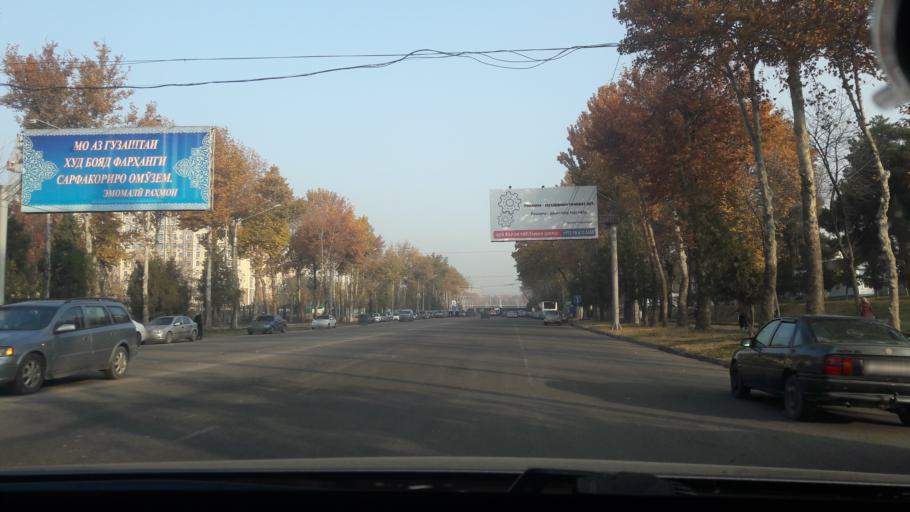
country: TJ
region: Dushanbe
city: Dushanbe
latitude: 38.5785
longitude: 68.7550
